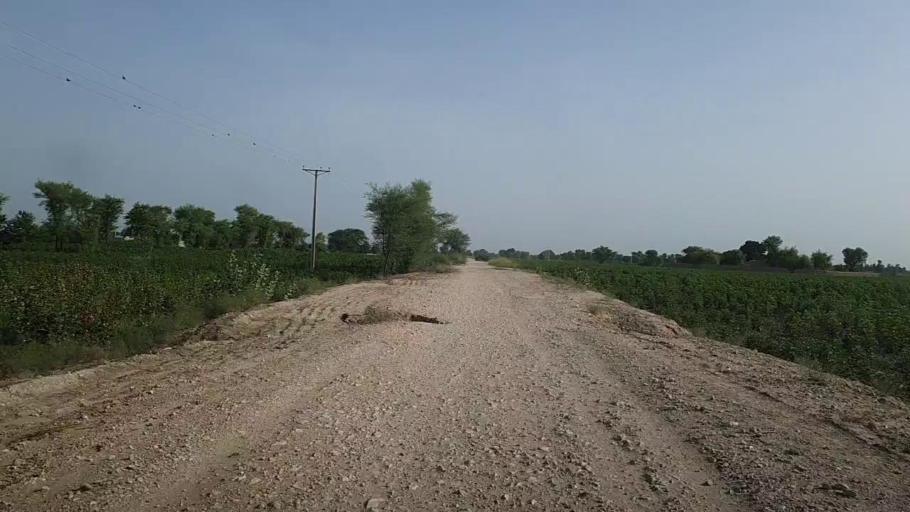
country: PK
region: Sindh
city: Pad Idan
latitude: 26.7625
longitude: 68.2572
